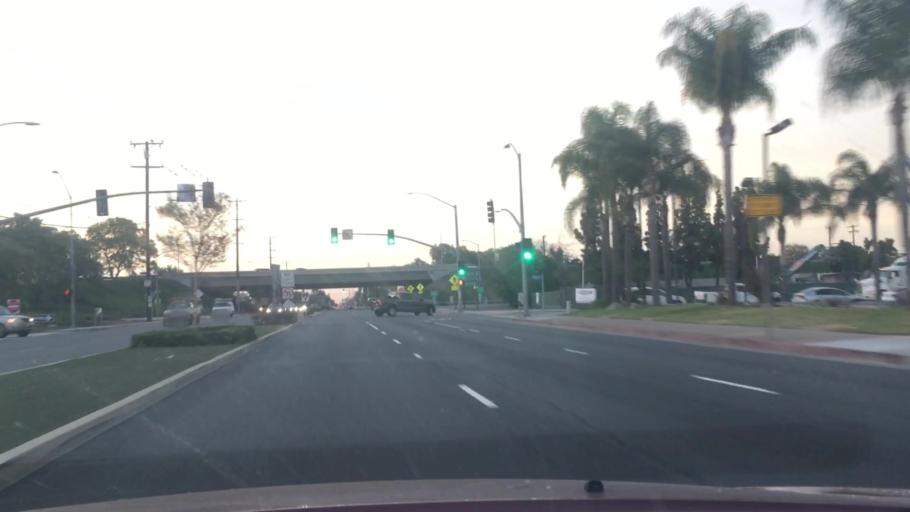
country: US
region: California
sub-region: Orange County
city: Buena Park
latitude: 33.8577
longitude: -118.0113
